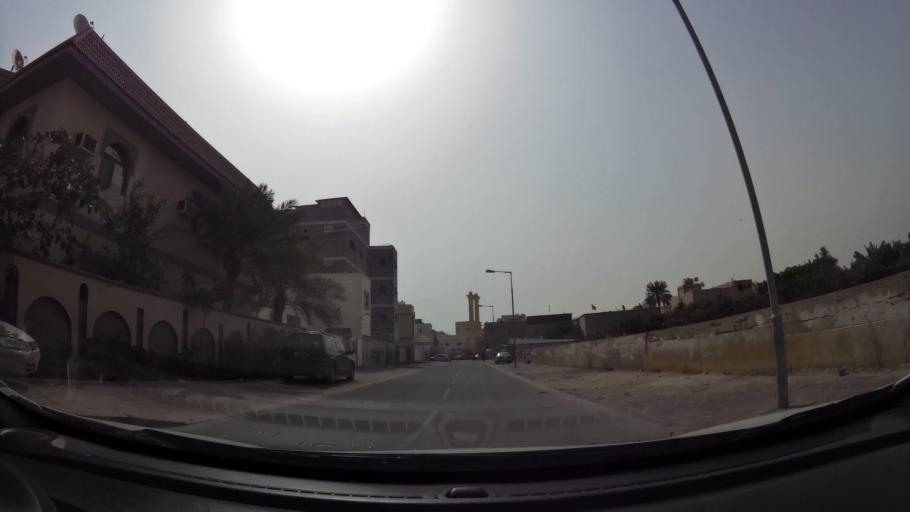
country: BH
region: Manama
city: Jidd Hafs
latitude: 26.2322
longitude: 50.5277
